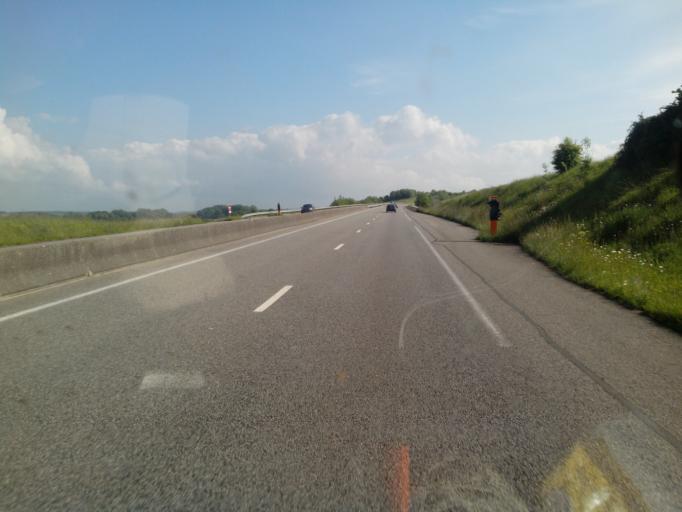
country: FR
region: Haute-Normandie
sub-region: Departement de la Seine-Maritime
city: Foucarmont
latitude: 49.8536
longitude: 1.5532
